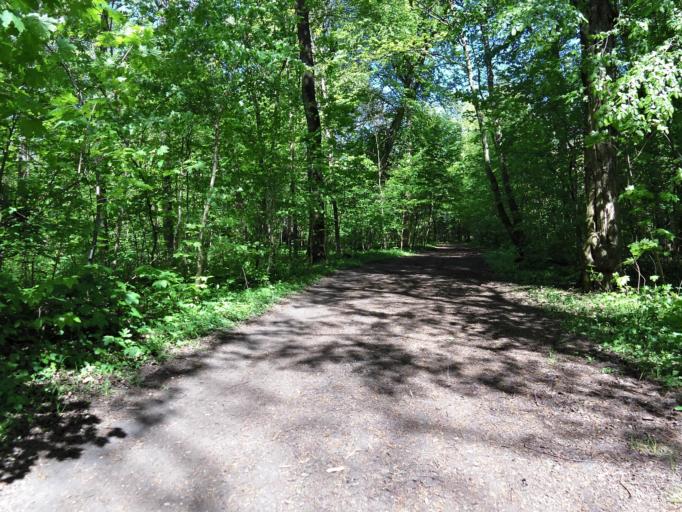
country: DE
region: Saxony
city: Leipzig
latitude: 51.3551
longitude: 12.3492
